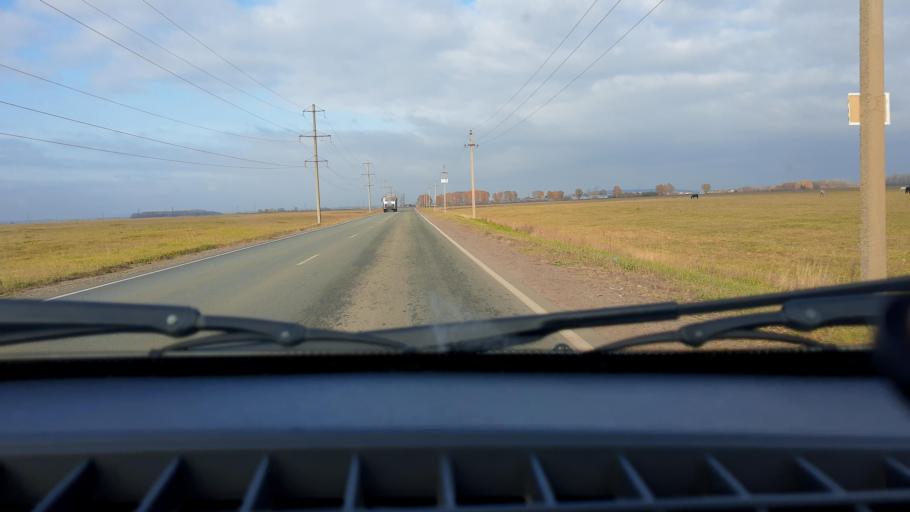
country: RU
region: Bashkortostan
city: Kabakovo
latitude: 54.5392
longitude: 56.0630
